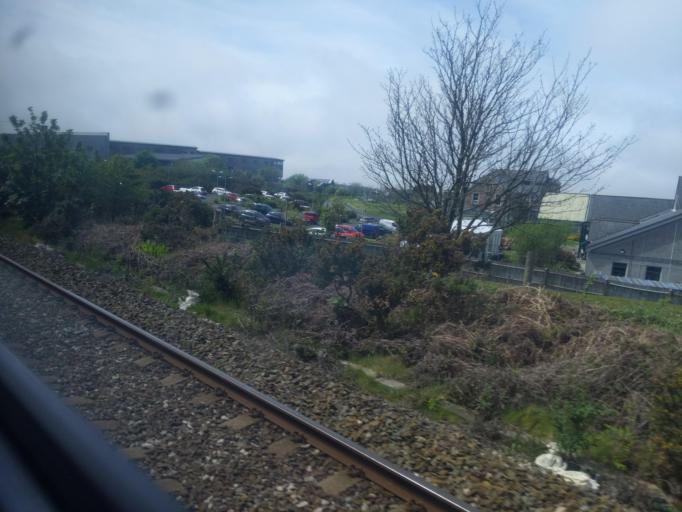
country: GB
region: England
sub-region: Cornwall
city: Redruth
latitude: 50.2280
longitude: -5.2440
